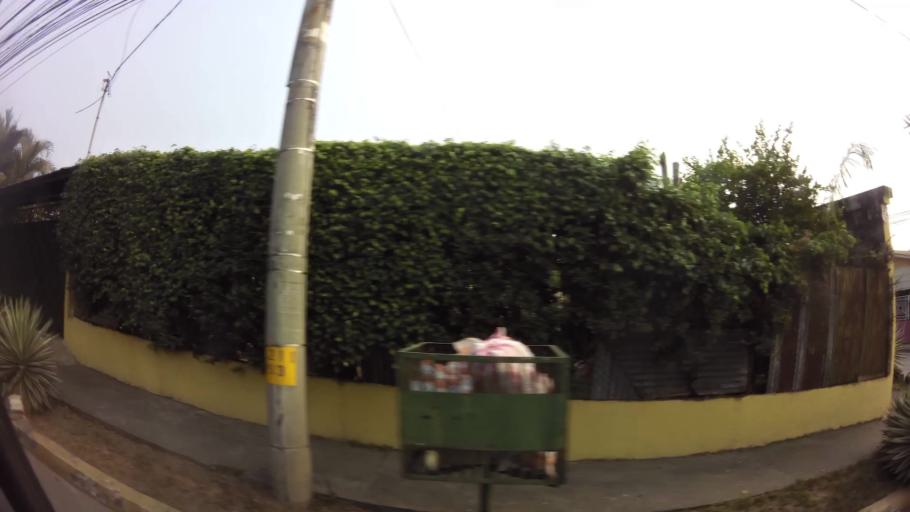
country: HN
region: Cortes
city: Armenta
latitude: 15.4984
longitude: -88.0408
